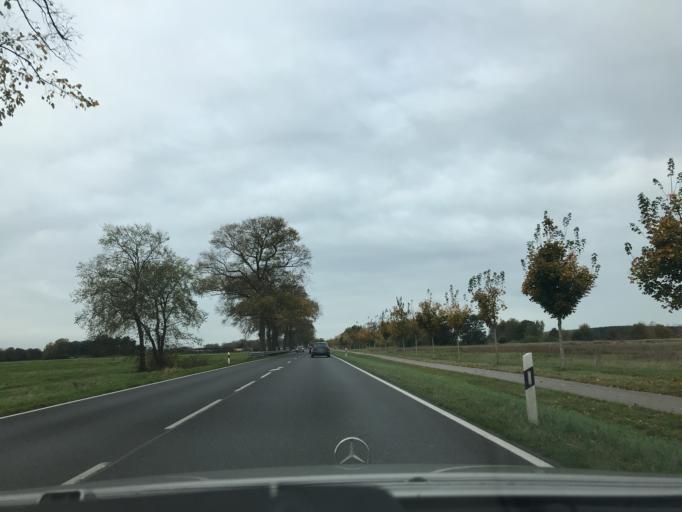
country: DE
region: Mecklenburg-Vorpommern
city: Ostseebad Zinnowitz
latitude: 54.0693
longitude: 13.8865
